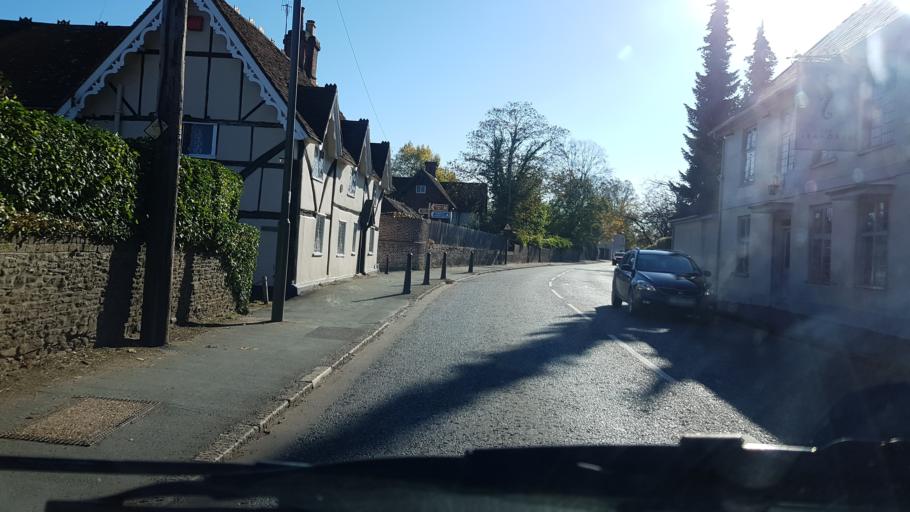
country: GB
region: England
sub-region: Surrey
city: Shalford
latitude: 51.2191
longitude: -0.5691
